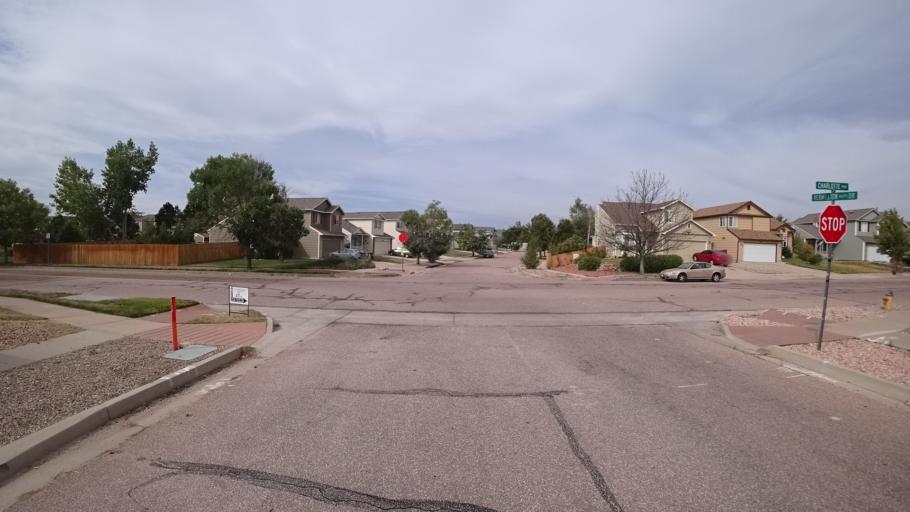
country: US
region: Colorado
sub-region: El Paso County
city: Cimarron Hills
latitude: 38.9122
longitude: -104.7115
